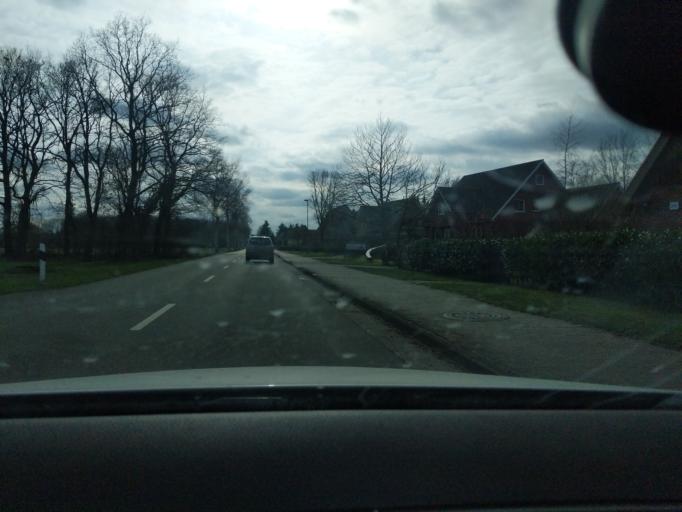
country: DE
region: Lower Saxony
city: Himmelpforten
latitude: 53.6298
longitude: 9.3207
